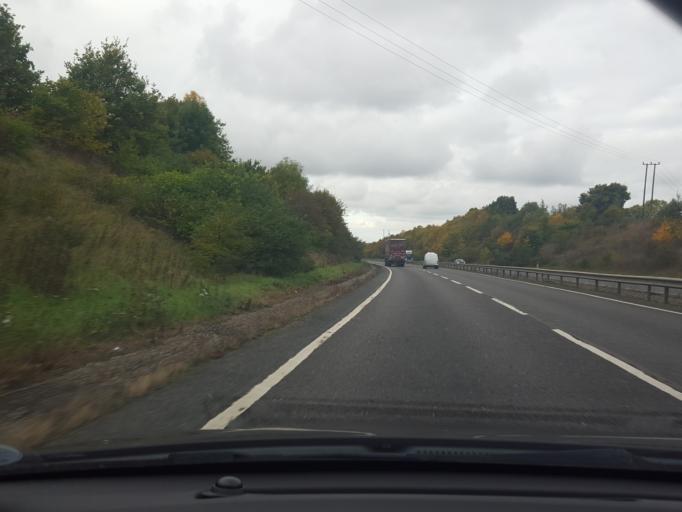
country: GB
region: England
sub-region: Suffolk
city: Stowmarket
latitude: 52.1960
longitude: 1.0077
